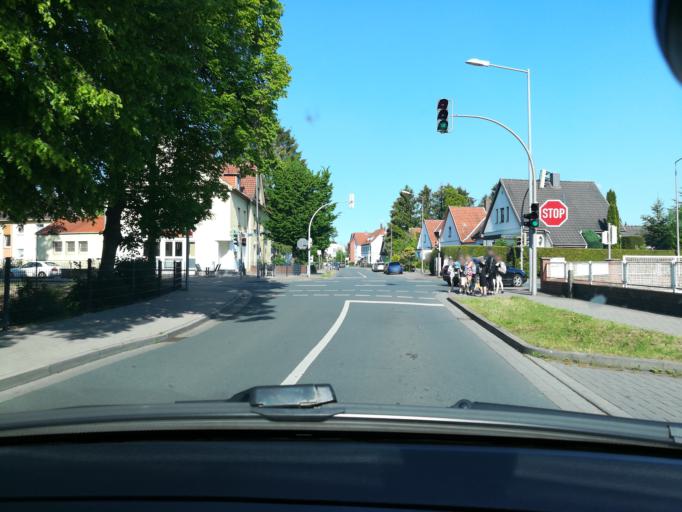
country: DE
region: North Rhine-Westphalia
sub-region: Regierungsbezirk Detmold
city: Minden
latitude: 52.2839
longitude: 8.8918
